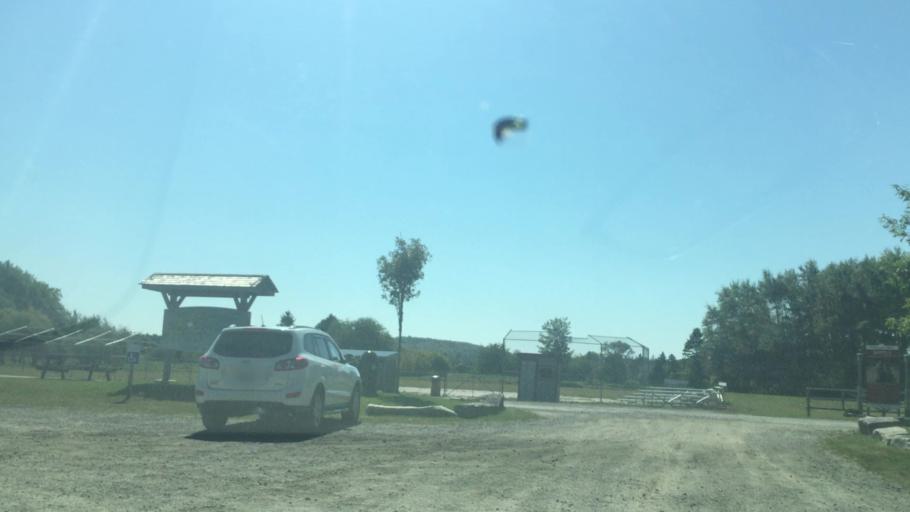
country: CA
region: Nova Scotia
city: Antigonish
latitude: 45.1379
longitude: -61.9831
